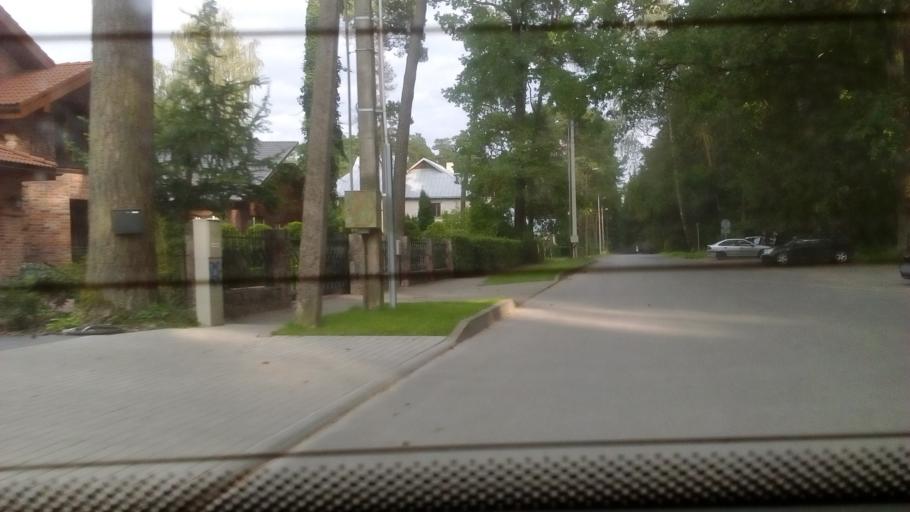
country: LT
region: Alytaus apskritis
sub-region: Alytus
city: Alytus
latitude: 54.3934
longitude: 24.0641
